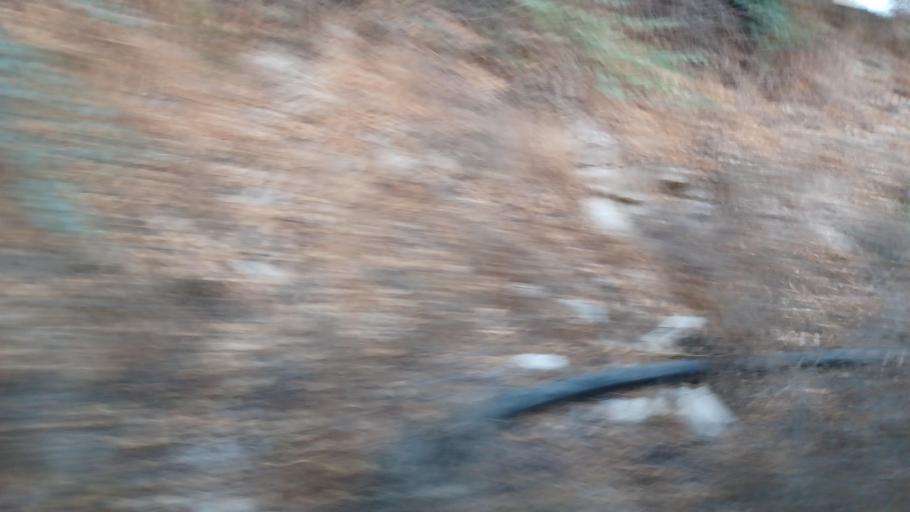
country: CY
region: Pafos
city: Mesogi
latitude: 34.8614
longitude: 32.5193
